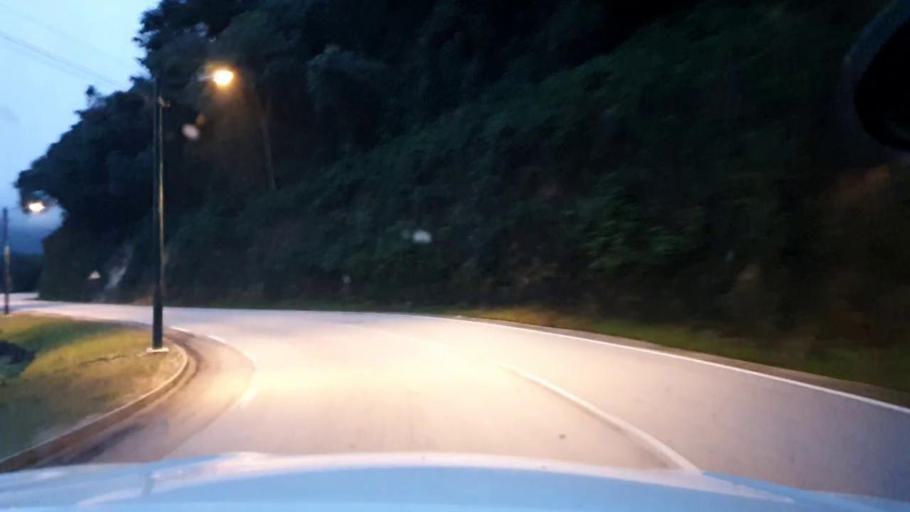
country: RW
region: Southern Province
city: Nzega
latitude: -2.5305
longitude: 29.3823
